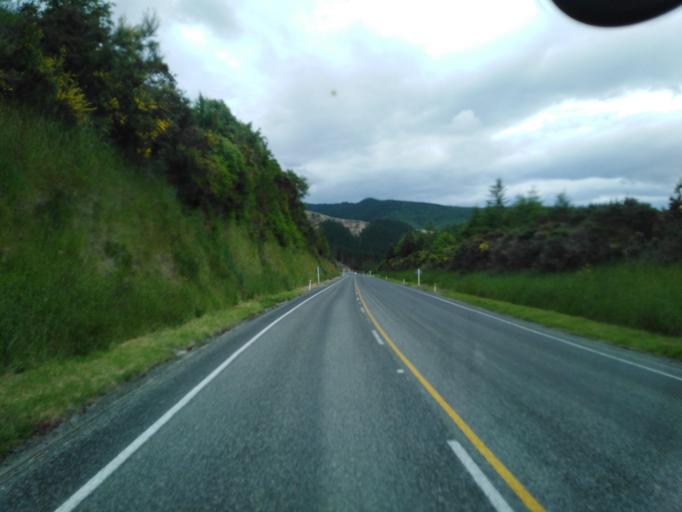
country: NZ
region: Tasman
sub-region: Tasman District
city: Wakefield
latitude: -41.4844
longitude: 172.9049
